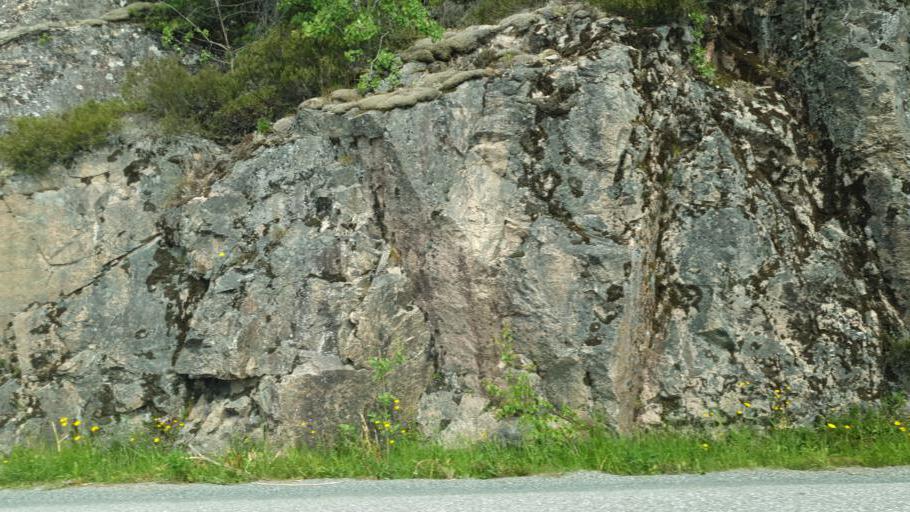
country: NO
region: Sor-Trondelag
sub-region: Trondheim
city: Trondheim
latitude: 63.5920
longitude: 10.4397
